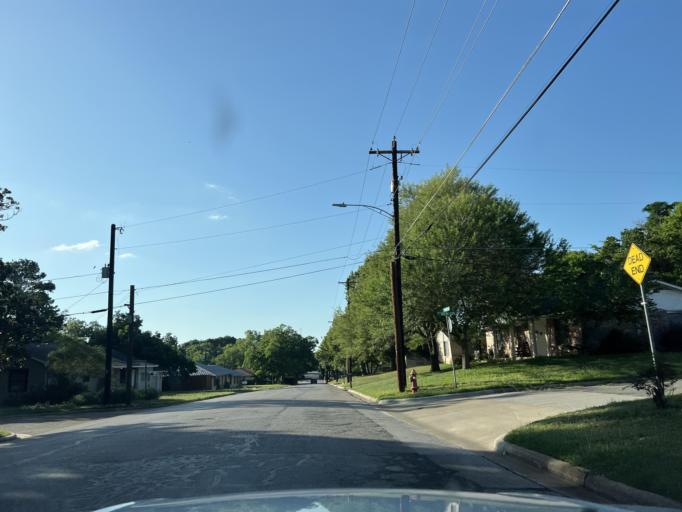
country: US
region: Texas
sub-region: Washington County
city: Brenham
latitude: 30.1594
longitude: -96.3876
